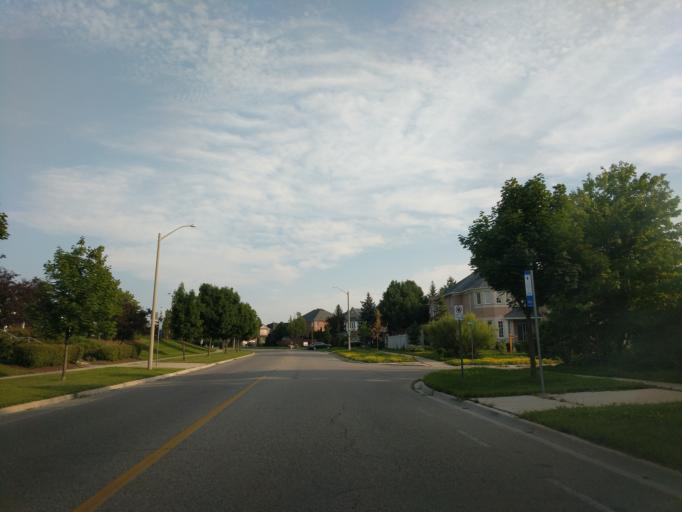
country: CA
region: Ontario
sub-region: York
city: Richmond Hill
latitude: 43.8834
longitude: -79.4027
